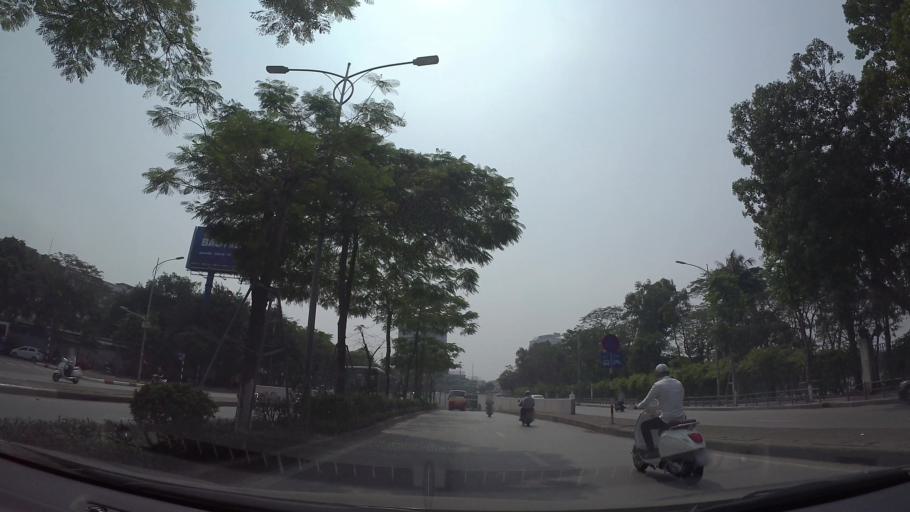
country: VN
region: Ha Noi
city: Hai BaTrung
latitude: 21.0078
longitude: 105.8441
